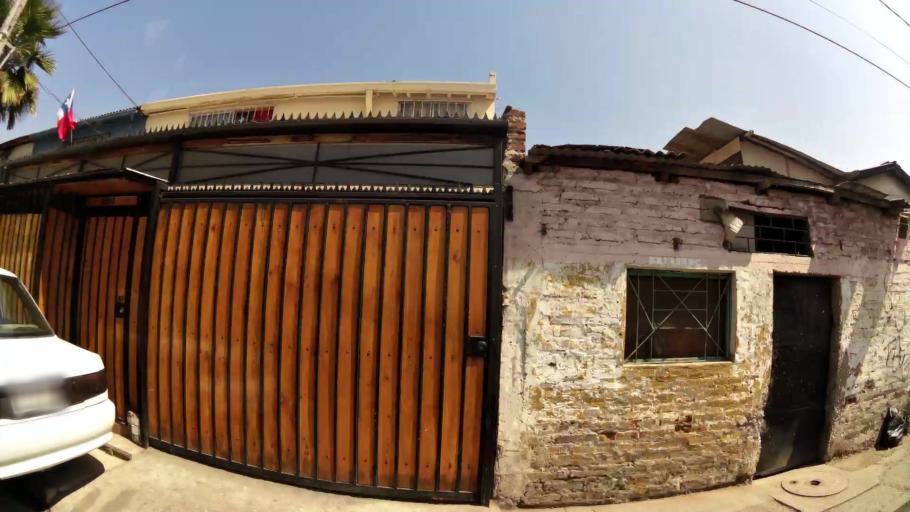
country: CL
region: Santiago Metropolitan
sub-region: Provincia de Santiago
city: La Pintana
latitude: -33.5576
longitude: -70.6138
